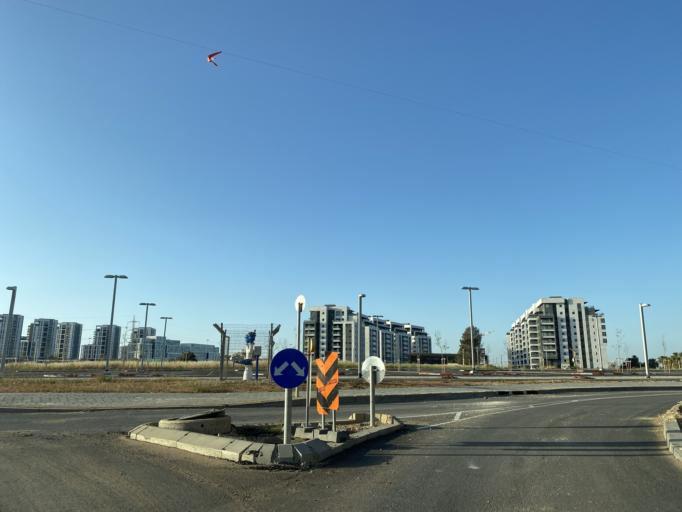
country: IL
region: Tel Aviv
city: Herzliyya
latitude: 32.1553
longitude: 34.8172
